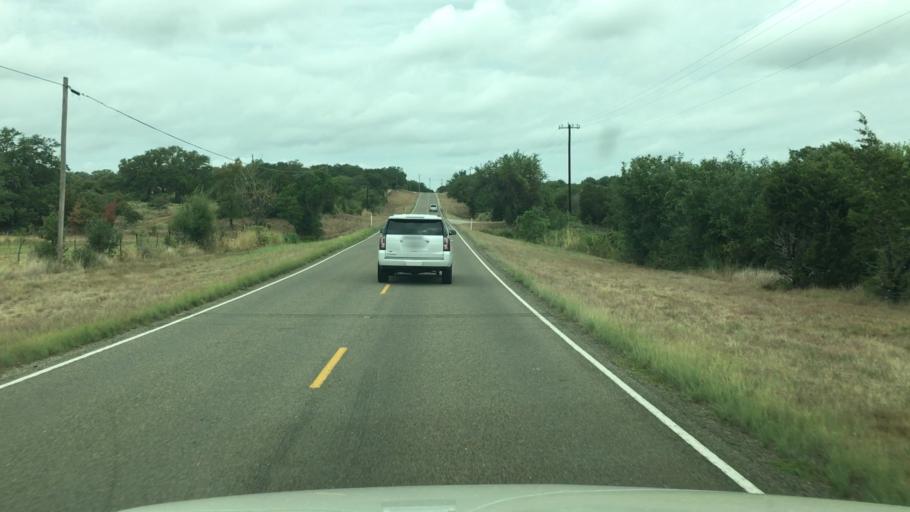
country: US
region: Texas
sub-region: Llano County
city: Horseshoe Bay
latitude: 30.4628
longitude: -98.4058
